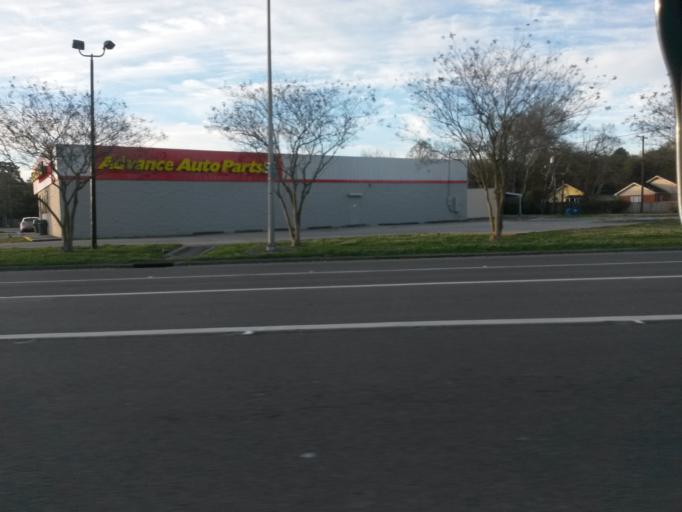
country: US
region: Louisiana
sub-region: Lafayette Parish
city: Lafayette
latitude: 30.2324
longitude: -92.0331
